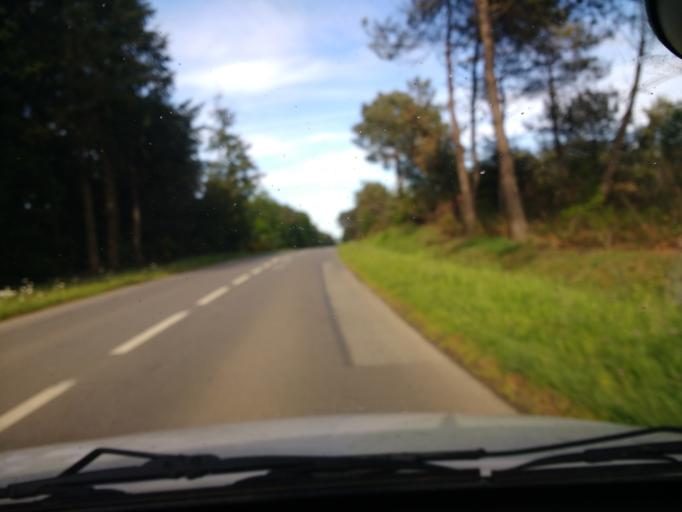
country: FR
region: Brittany
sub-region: Departement du Morbihan
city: Pluherlin
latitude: 47.7065
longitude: -2.3551
